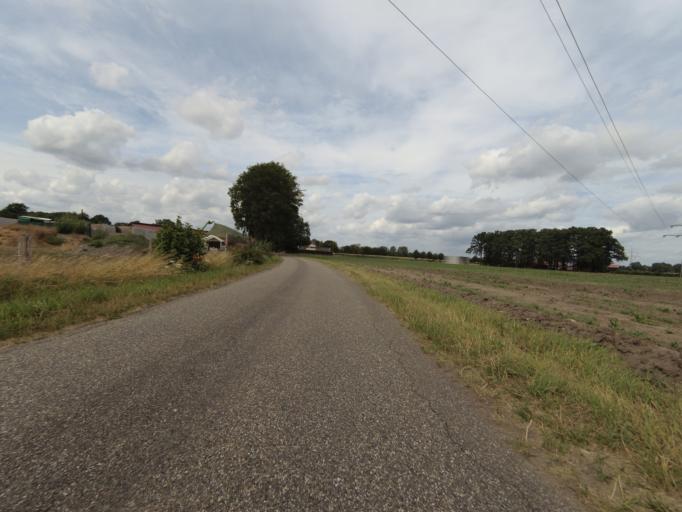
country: DE
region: North Rhine-Westphalia
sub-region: Regierungsbezirk Munster
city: Ahaus
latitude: 52.1228
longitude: 7.0097
